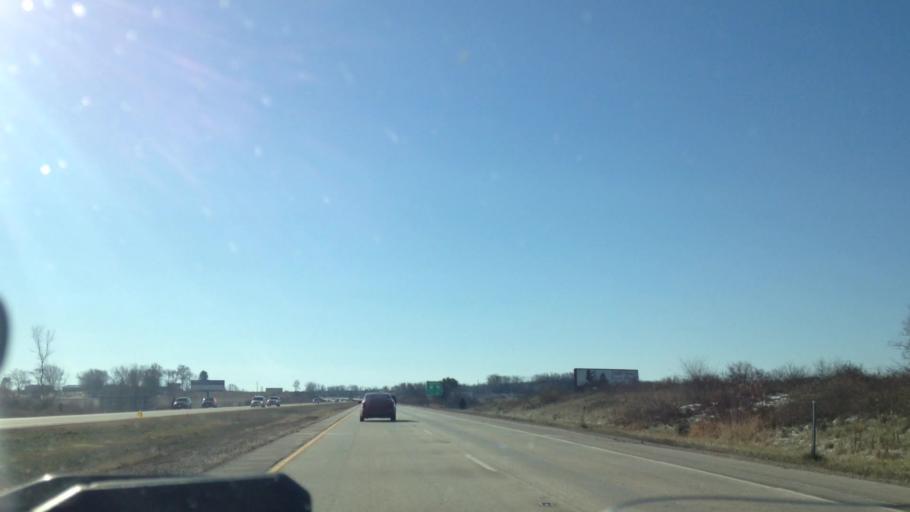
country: US
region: Wisconsin
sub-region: Washington County
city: Jackson
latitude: 43.3023
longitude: -88.1865
